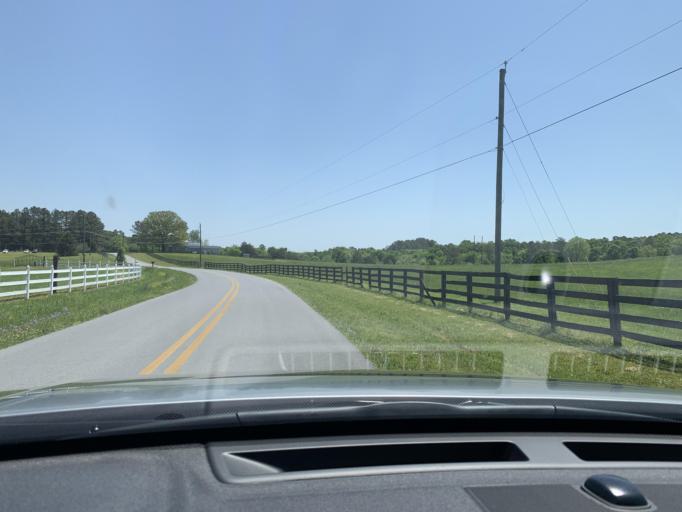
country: US
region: Georgia
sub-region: Polk County
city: Aragon
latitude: 34.0689
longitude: -85.0906
